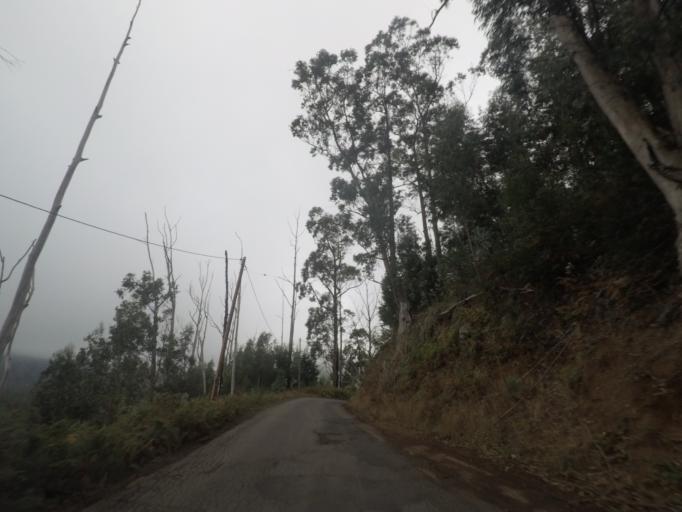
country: PT
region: Madeira
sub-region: Funchal
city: Nossa Senhora do Monte
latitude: 32.6908
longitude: -16.9077
